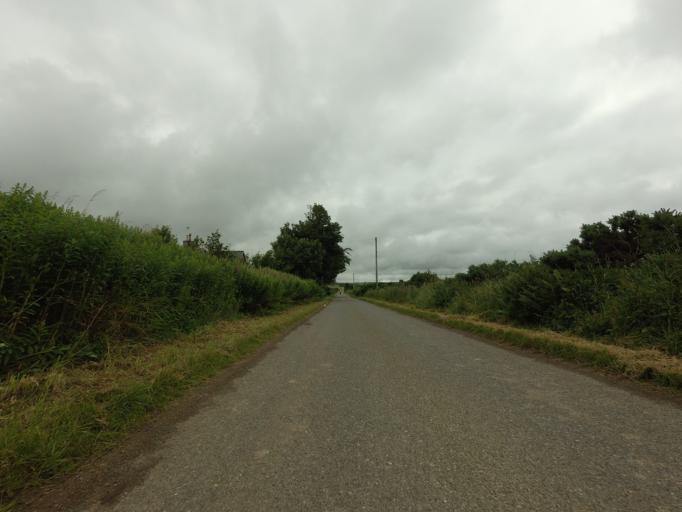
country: GB
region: Scotland
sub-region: Aberdeenshire
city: Turriff
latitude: 57.5455
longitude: -2.2890
